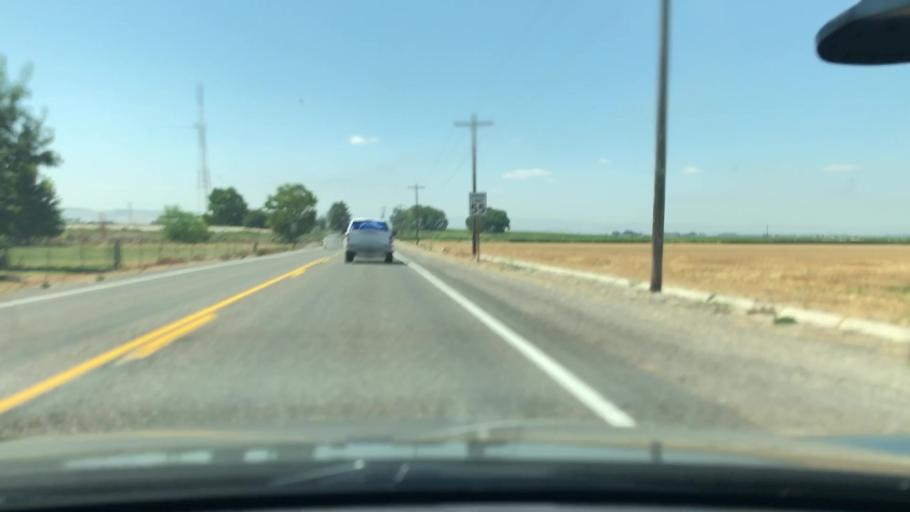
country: US
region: Idaho
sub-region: Owyhee County
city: Marsing
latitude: 43.5453
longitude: -116.8575
